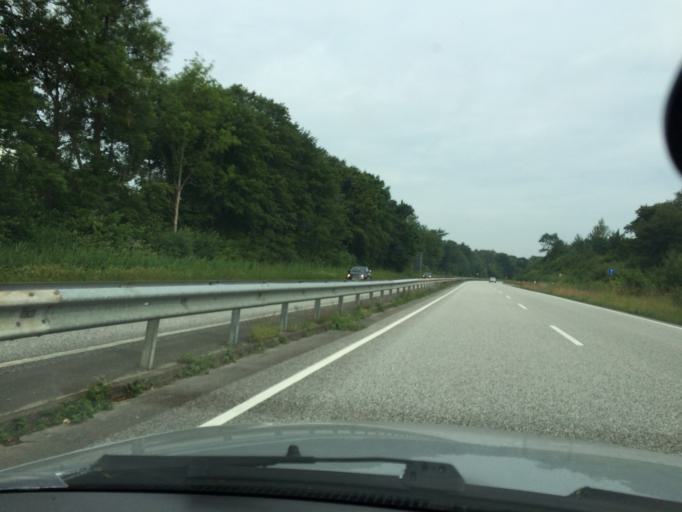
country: DE
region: Schleswig-Holstein
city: Harrislee
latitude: 54.8009
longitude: 9.4080
